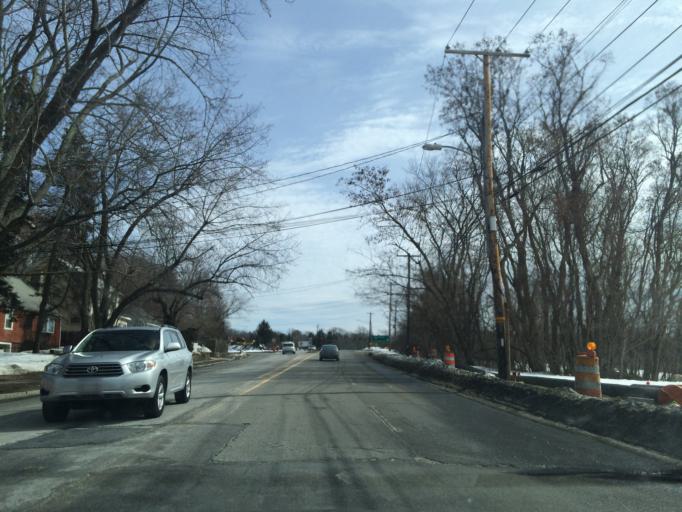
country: US
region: Massachusetts
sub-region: Middlesex County
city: Bedford
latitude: 42.4731
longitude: -71.2475
